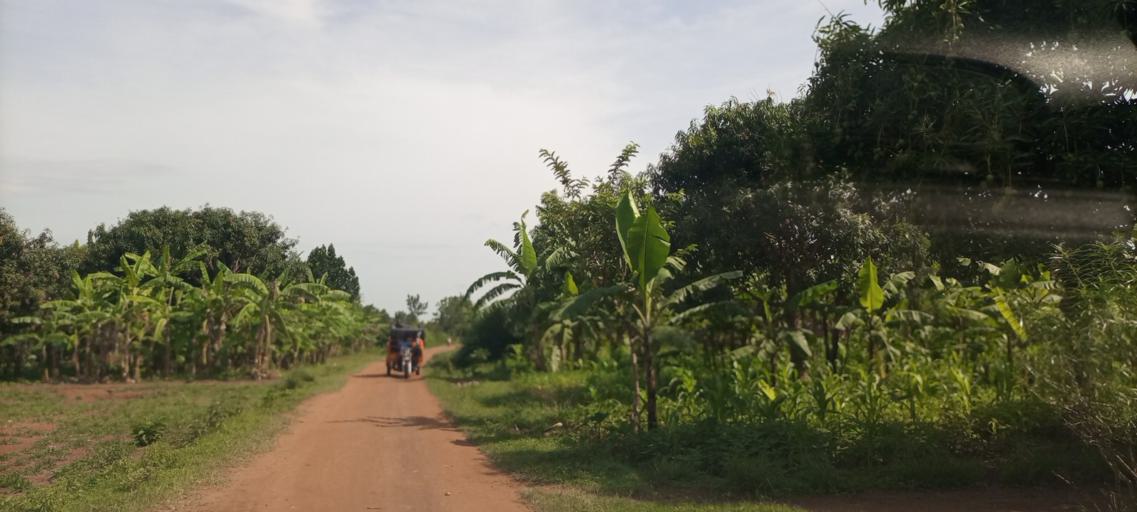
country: UG
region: Eastern Region
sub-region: Budaka District
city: Budaka
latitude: 1.1314
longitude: 34.0225
